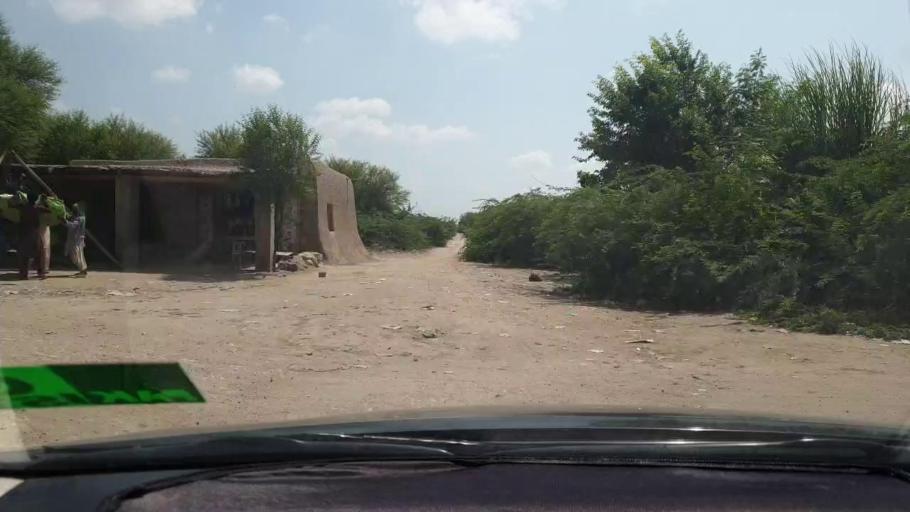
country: PK
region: Sindh
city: Naukot
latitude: 24.8848
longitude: 69.2240
